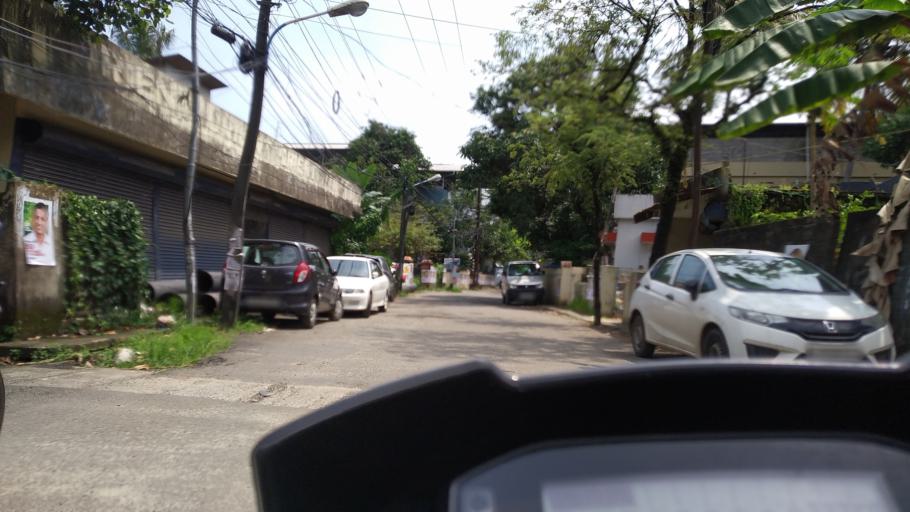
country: IN
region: Kerala
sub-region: Ernakulam
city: Cochin
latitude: 9.9597
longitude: 76.2917
